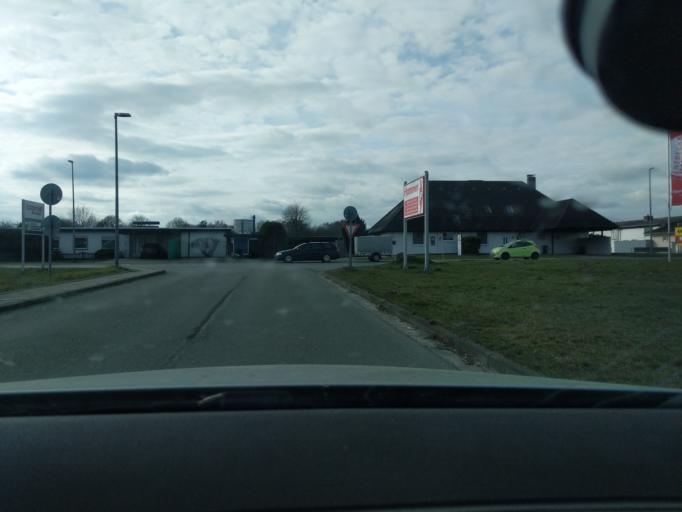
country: DE
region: Lower Saxony
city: Stade
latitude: 53.5926
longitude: 9.4241
